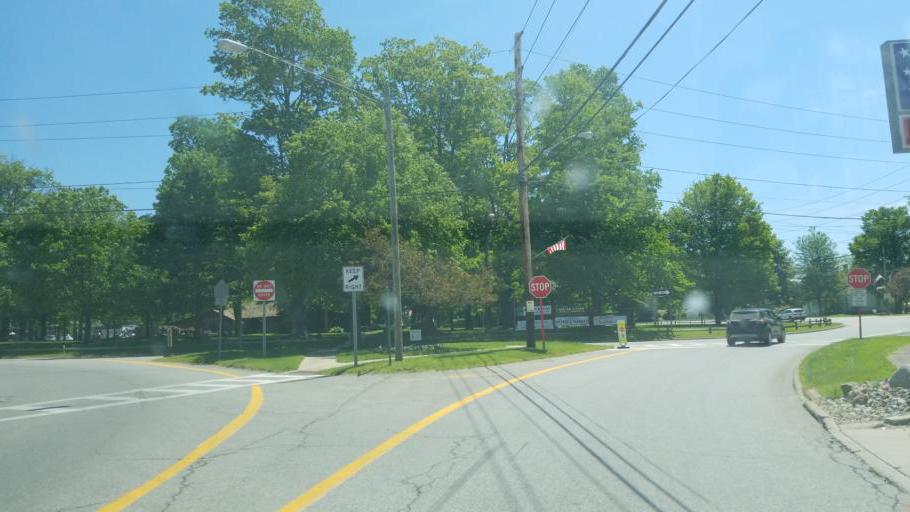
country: US
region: Ohio
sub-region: Geauga County
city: Burton
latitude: 41.4708
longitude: -81.1462
